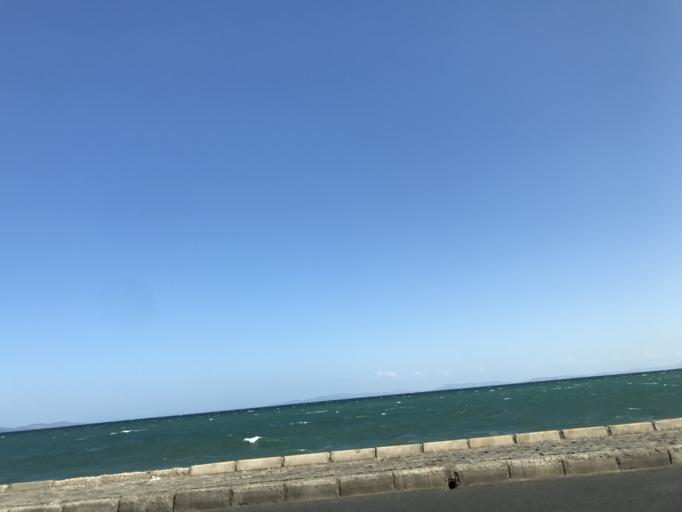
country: TR
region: Izmir
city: Urla
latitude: 38.3751
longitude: 26.8728
